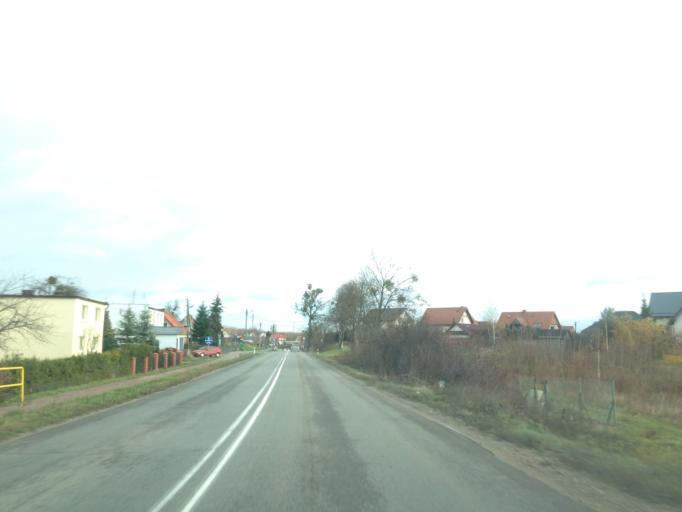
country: PL
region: Pomeranian Voivodeship
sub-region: Powiat gdanski
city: Lublewo Gdanskie
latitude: 54.2806
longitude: 18.4879
